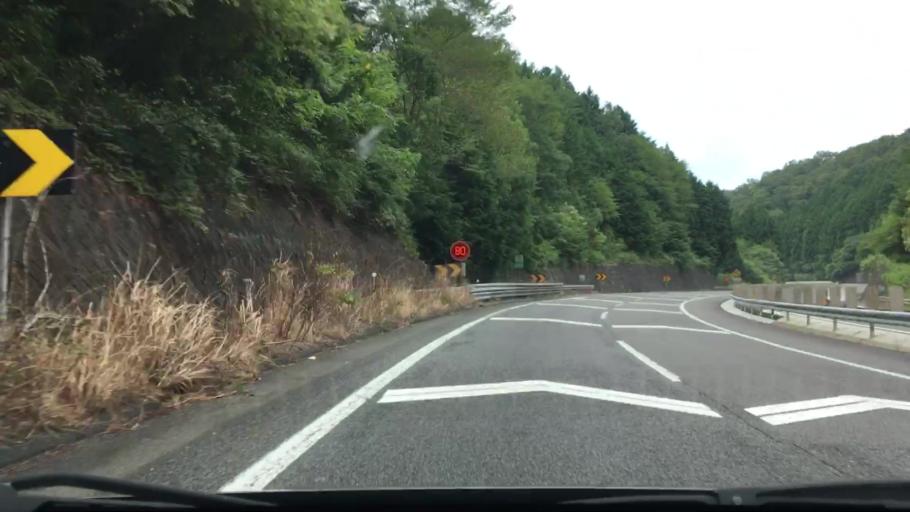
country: JP
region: Hiroshima
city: Shobara
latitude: 34.8908
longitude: 133.1988
